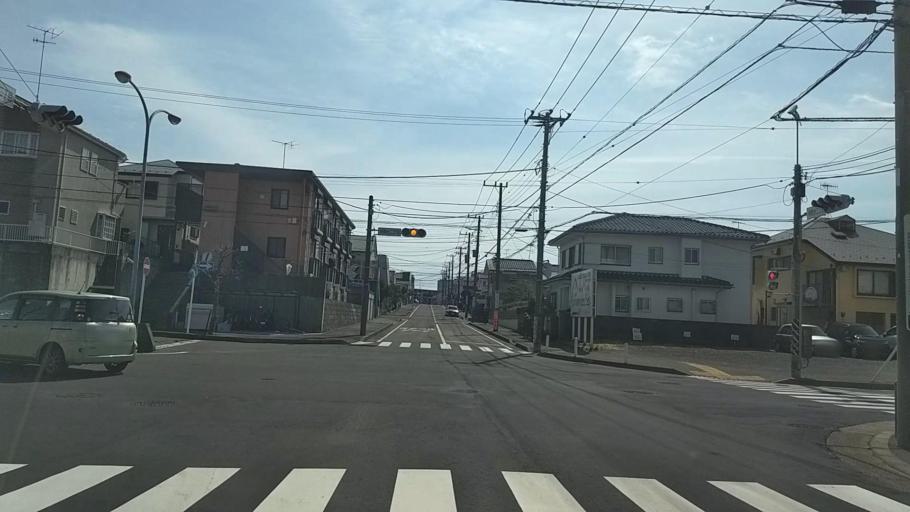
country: JP
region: Kanagawa
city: Fujisawa
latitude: 35.3927
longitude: 139.4661
